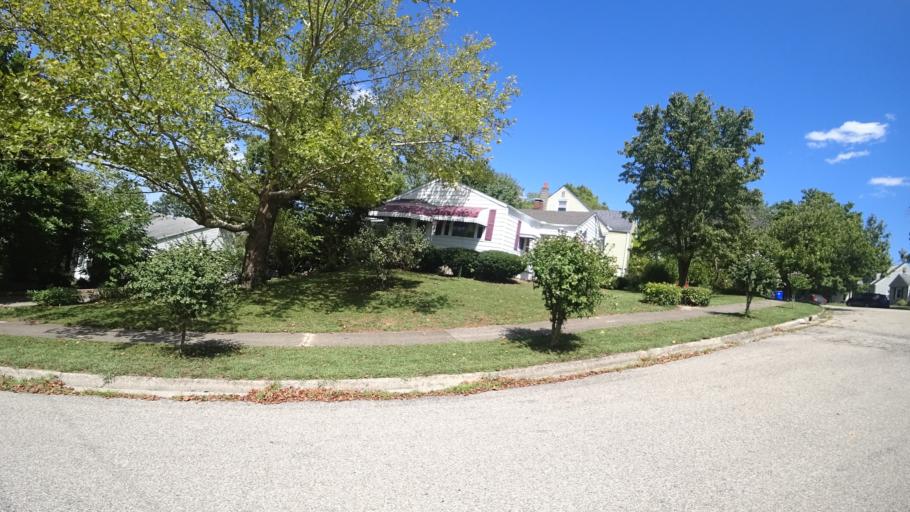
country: US
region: Ohio
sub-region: Butler County
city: New Miami
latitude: 39.4098
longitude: -84.5374
